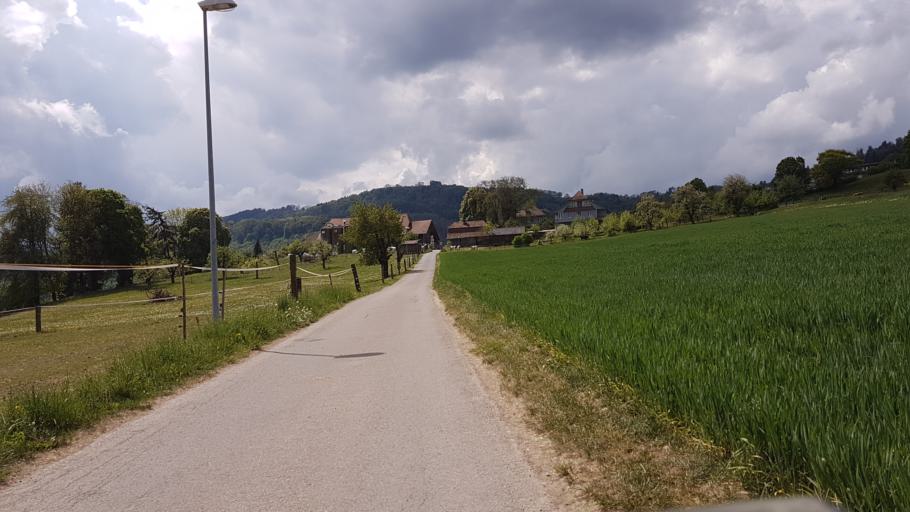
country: CH
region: Bern
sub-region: Bern-Mittelland District
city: Kehrsatz
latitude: 46.9195
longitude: 7.4781
